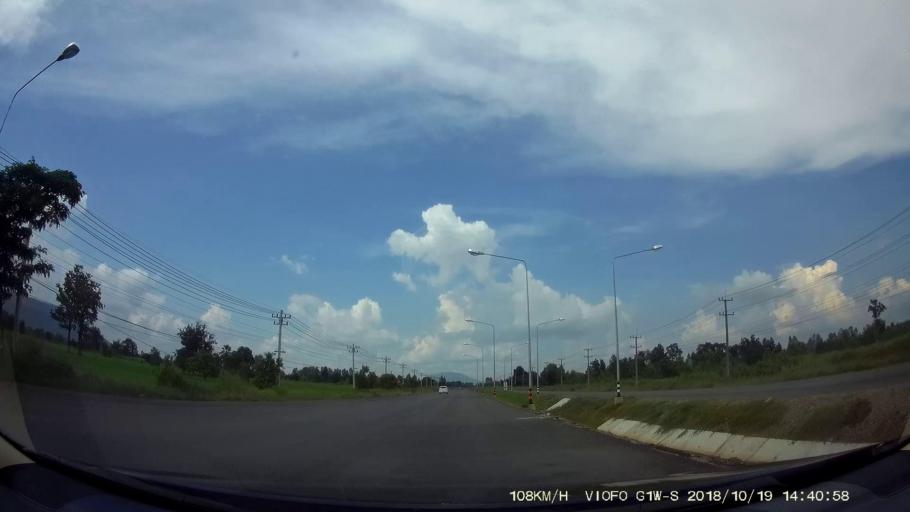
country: TH
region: Chaiyaphum
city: Phu Khiao
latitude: 16.2493
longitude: 102.1975
